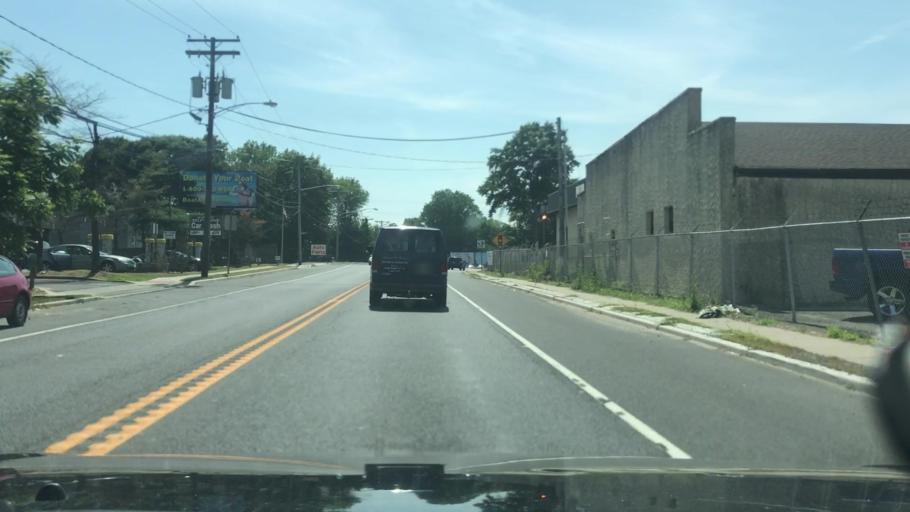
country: US
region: New Jersey
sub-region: Monmouth County
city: Long Branch
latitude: 40.3046
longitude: -74.0072
